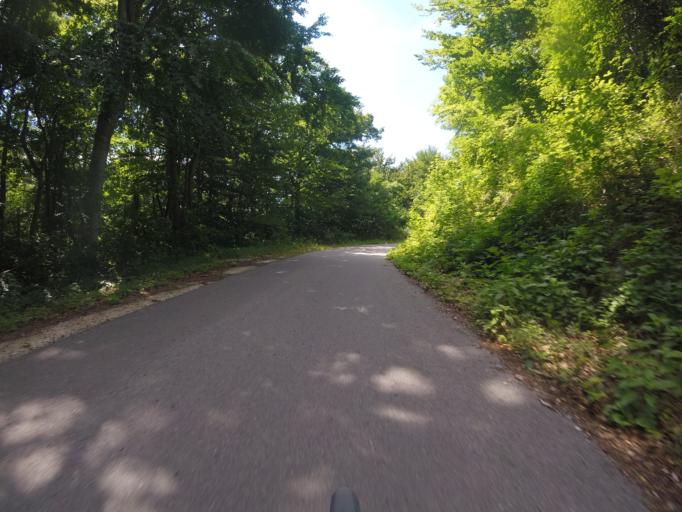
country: SI
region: Kostanjevica na Krki
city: Kostanjevica na Krki
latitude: 45.7696
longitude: 15.4122
